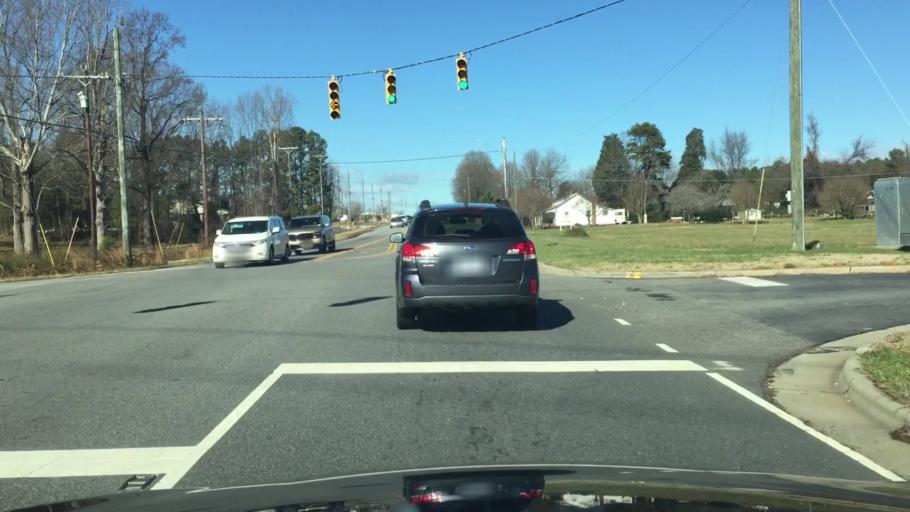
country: US
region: North Carolina
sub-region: Iredell County
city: Mooresville
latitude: 35.5780
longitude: -80.8712
